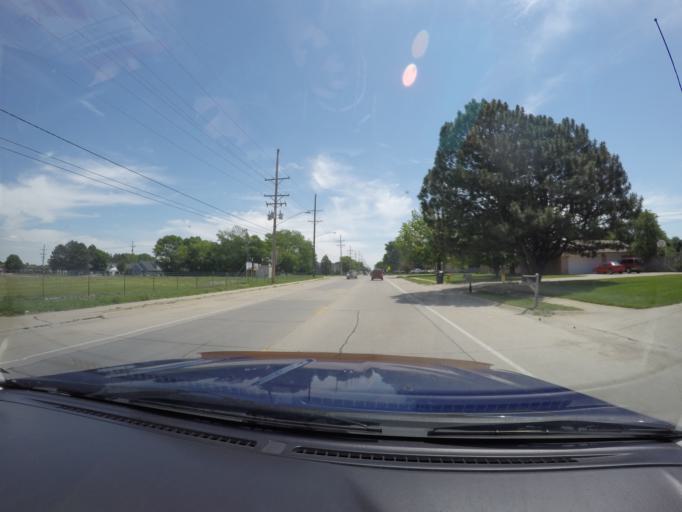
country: US
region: Nebraska
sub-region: Hall County
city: Grand Island
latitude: 40.9022
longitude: -98.3479
